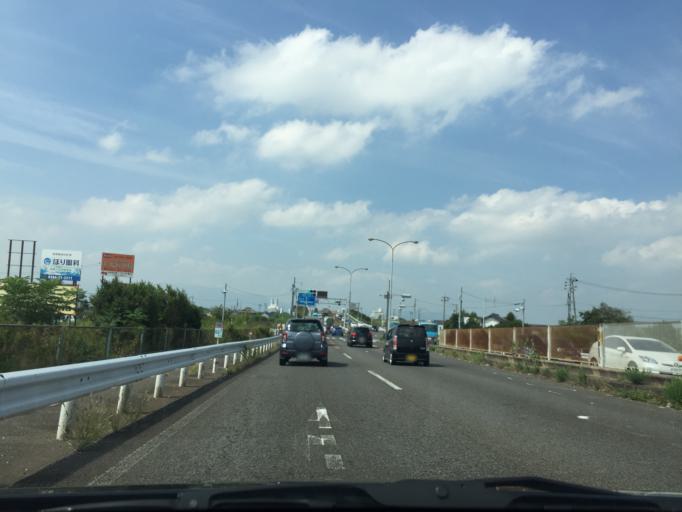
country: JP
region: Gifu
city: Ogaki
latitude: 35.3776
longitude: 136.6632
